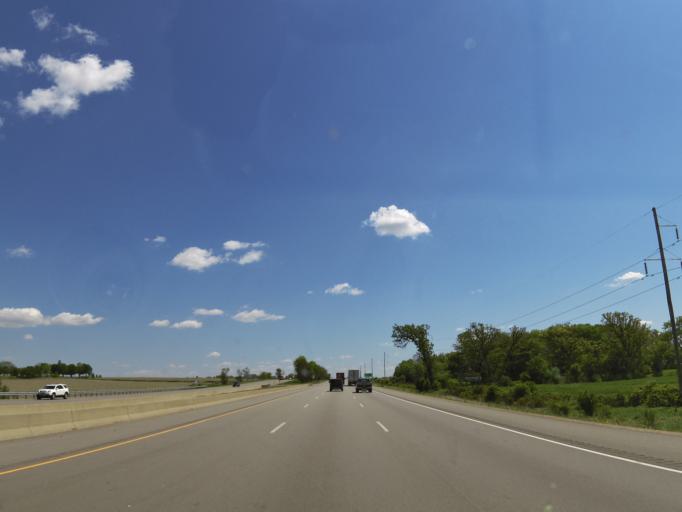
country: US
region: Wisconsin
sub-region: Dane County
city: De Forest
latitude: 43.2421
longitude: -89.3731
